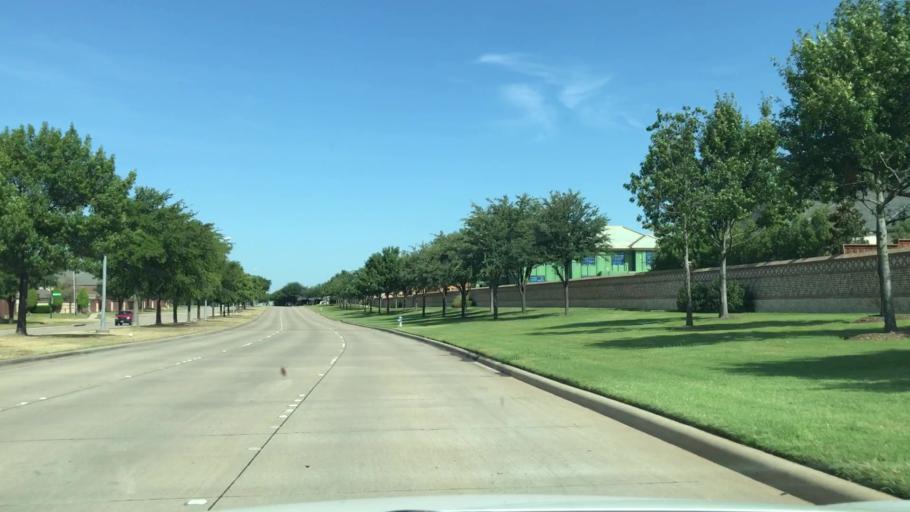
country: US
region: Texas
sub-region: Denton County
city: The Colony
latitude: 33.0676
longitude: -96.8401
